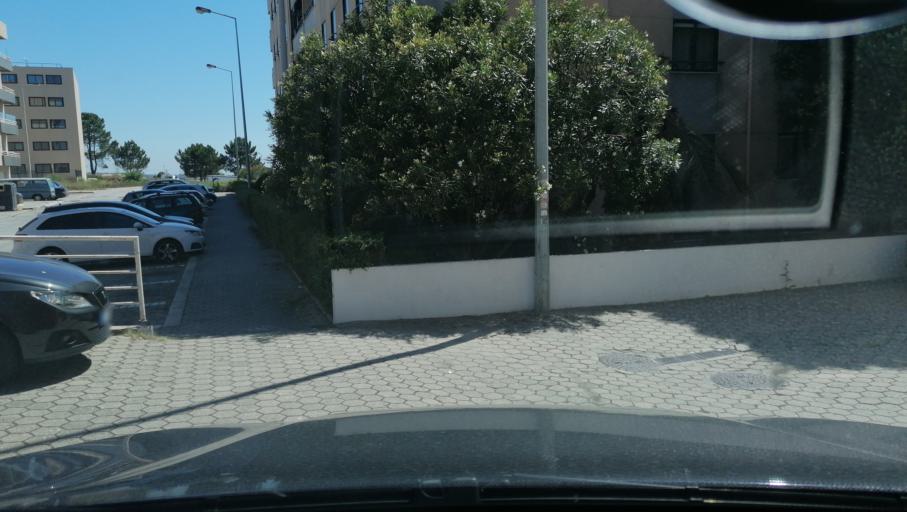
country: PT
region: Porto
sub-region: Vila Nova de Gaia
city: Canidelo
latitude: 41.1300
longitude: -8.6498
